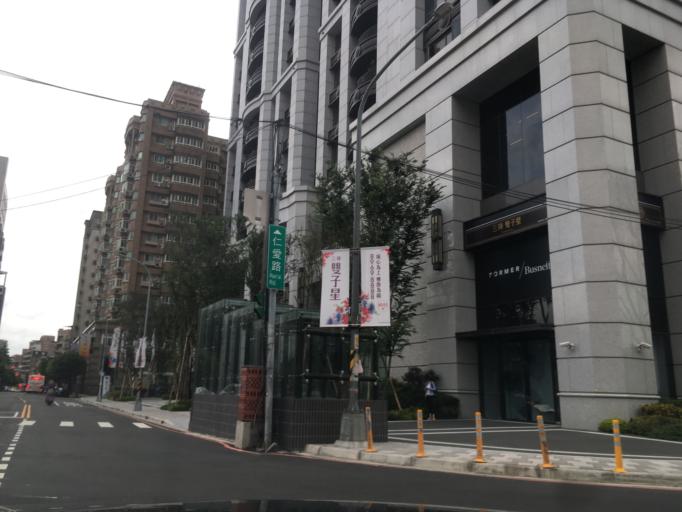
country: TW
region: Taipei
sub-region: Taipei
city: Banqiao
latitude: 25.0091
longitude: 121.5049
